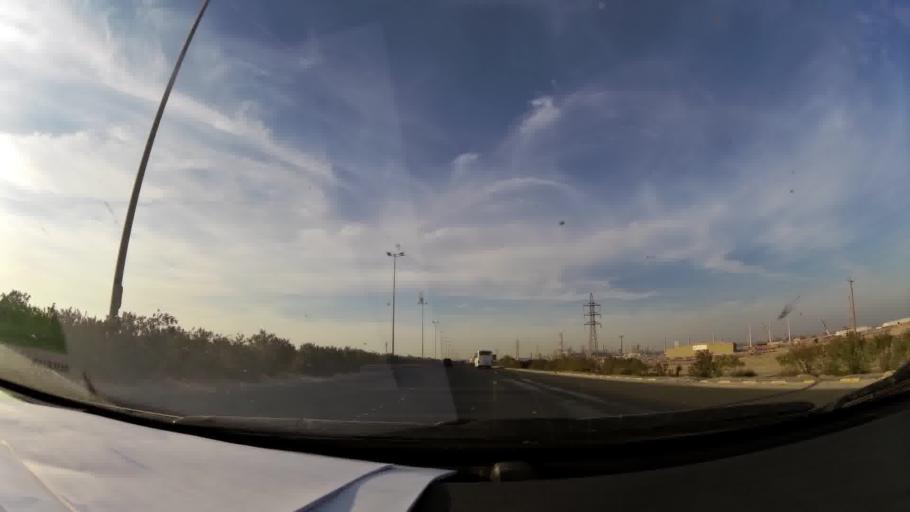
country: KW
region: Al Ahmadi
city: Al Fahahil
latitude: 28.9787
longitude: 48.1568
